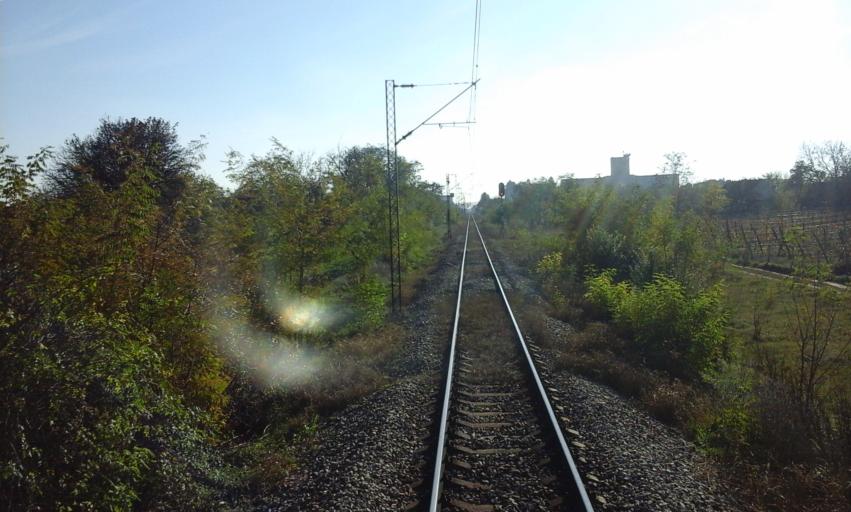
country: RS
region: Autonomna Pokrajina Vojvodina
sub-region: Severnobacki Okrug
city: Backa Topola
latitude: 45.8242
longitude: 19.6505
